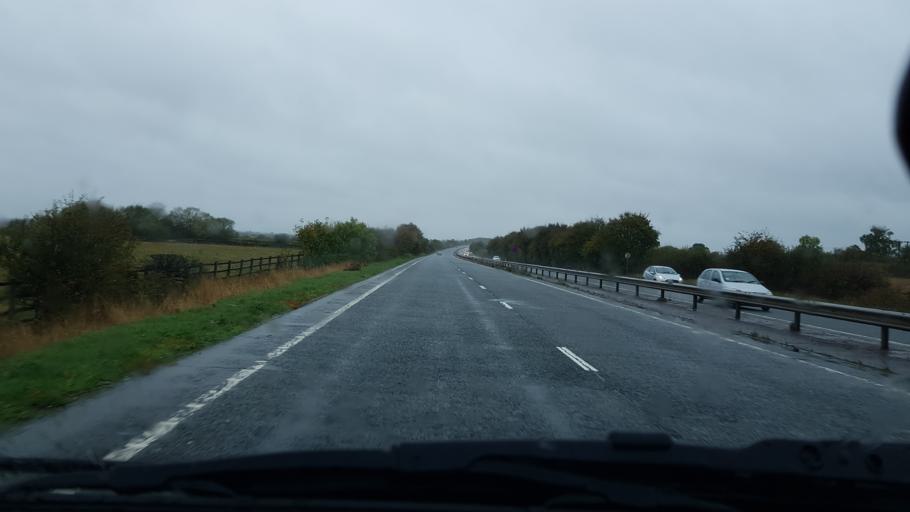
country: GB
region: England
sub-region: Oxfordshire
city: Carterton
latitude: 51.7835
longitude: -1.5571
